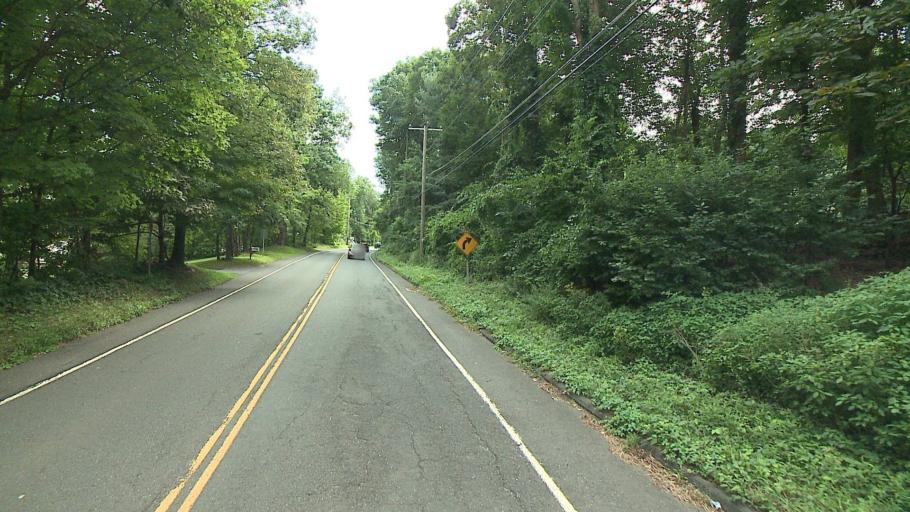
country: US
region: New York
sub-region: Putnam County
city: Putnam Lake
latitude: 41.4352
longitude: -73.4960
